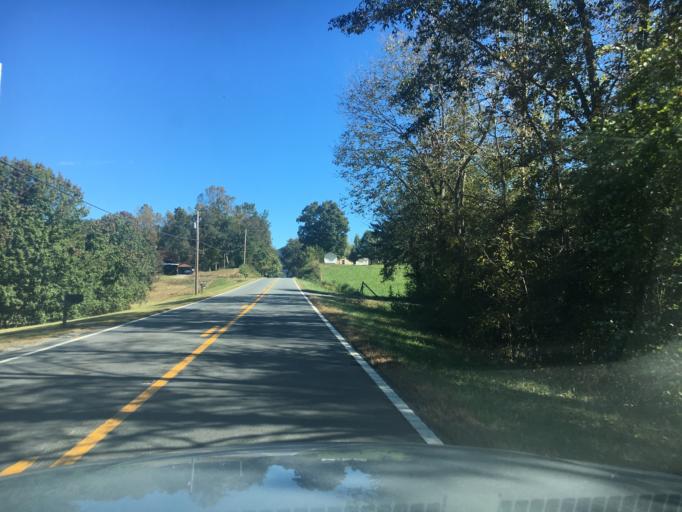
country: US
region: North Carolina
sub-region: Rutherford County
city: Spindale
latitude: 35.4841
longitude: -81.8752
